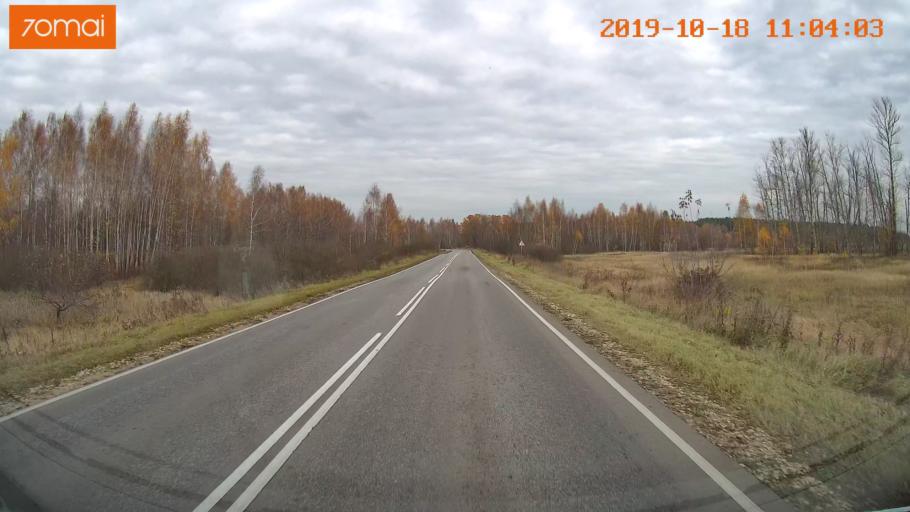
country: RU
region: Tula
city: Yepifan'
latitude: 53.8891
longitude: 38.5502
